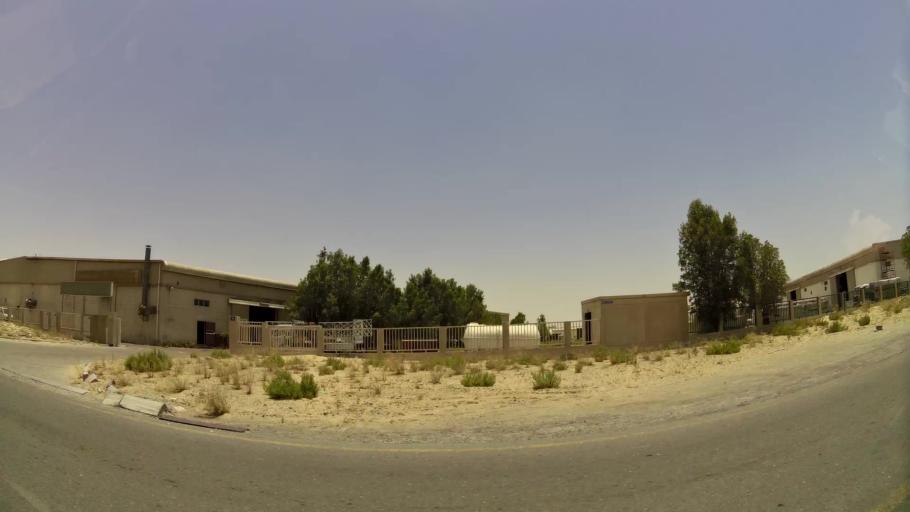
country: AE
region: Dubai
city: Dubai
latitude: 24.9847
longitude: 55.1678
